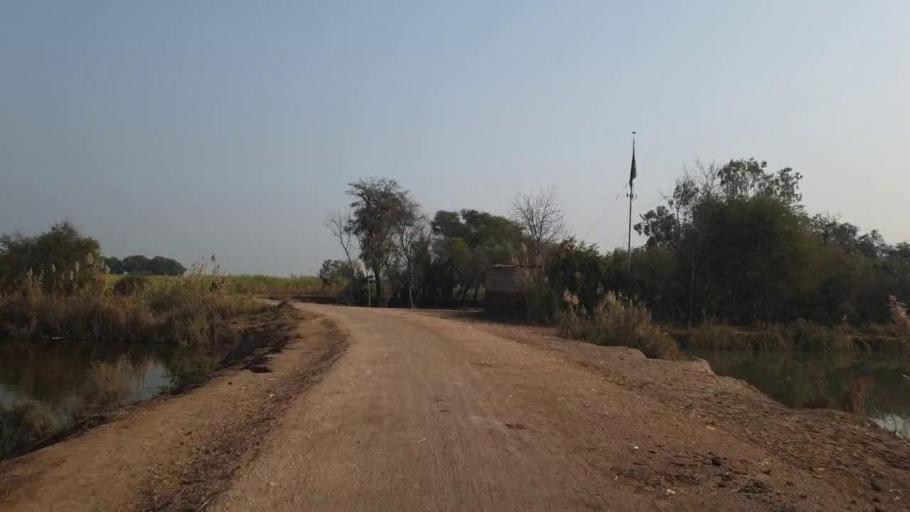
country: PK
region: Sindh
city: Shahdadpur
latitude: 25.9563
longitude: 68.5318
